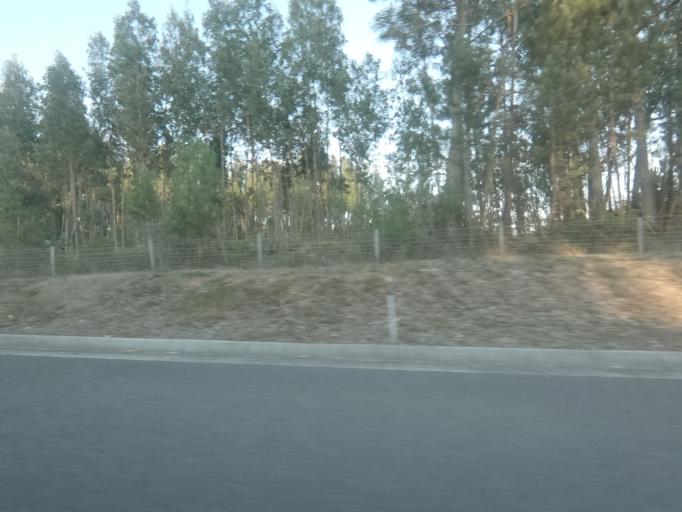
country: PT
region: Leiria
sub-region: Leiria
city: Santa Catarina da Serra
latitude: 39.6536
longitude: -8.6961
